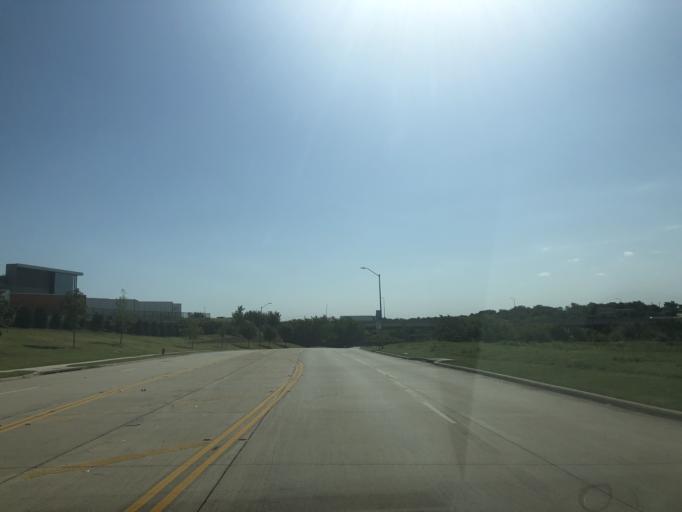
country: US
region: Texas
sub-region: Dallas County
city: Grand Prairie
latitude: 32.7508
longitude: -97.0319
